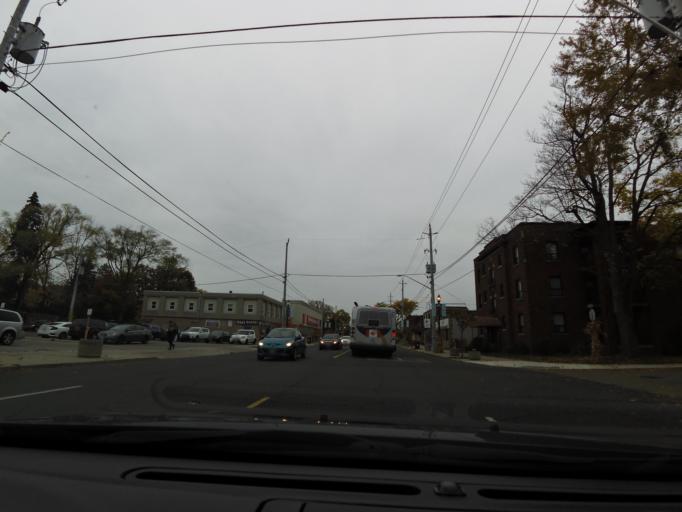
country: CA
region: Ontario
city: Hamilton
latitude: 43.2628
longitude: -79.9037
